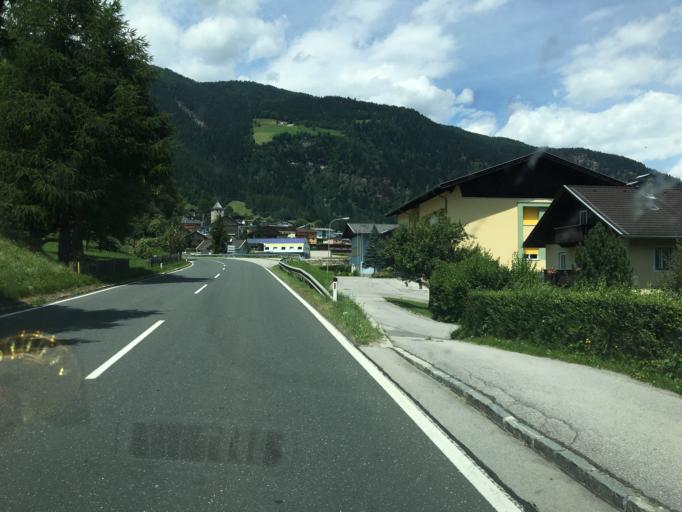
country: AT
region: Carinthia
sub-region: Politischer Bezirk Spittal an der Drau
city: Winklern
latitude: 46.8678
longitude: 12.8806
